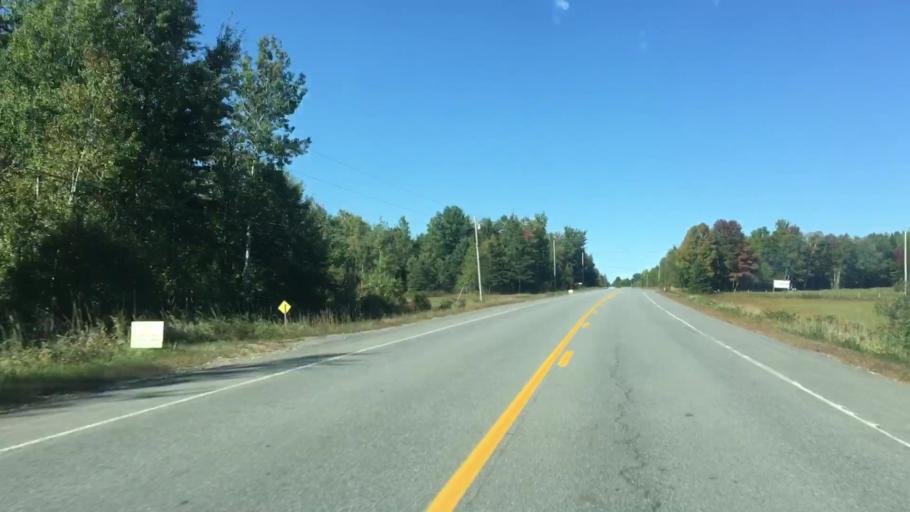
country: US
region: Maine
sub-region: Piscataquis County
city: Sangerville
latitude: 45.0703
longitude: -69.4589
